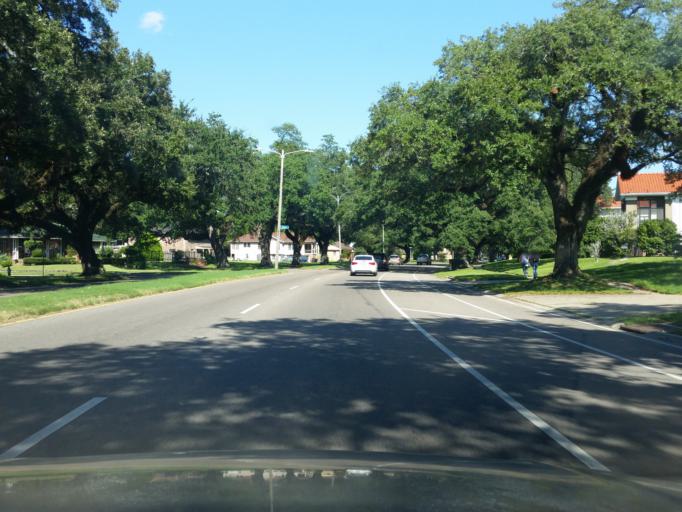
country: US
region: Louisiana
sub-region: Orleans Parish
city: New Orleans
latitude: 30.0026
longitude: -90.0545
